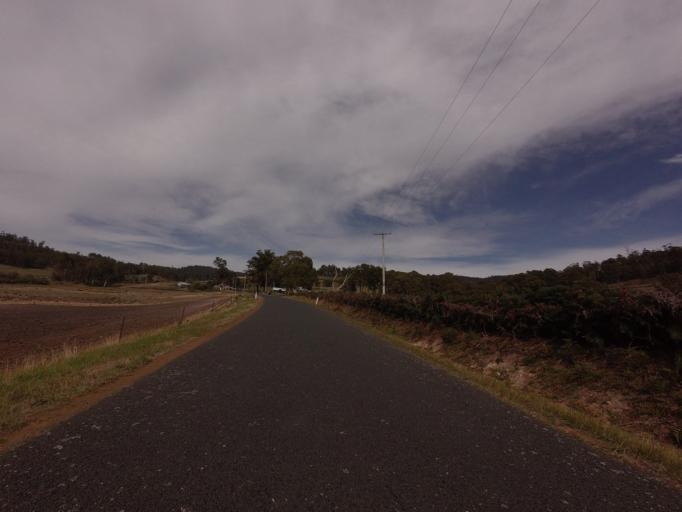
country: AU
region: Tasmania
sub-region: Sorell
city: Sorell
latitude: -42.4654
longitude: 147.5693
